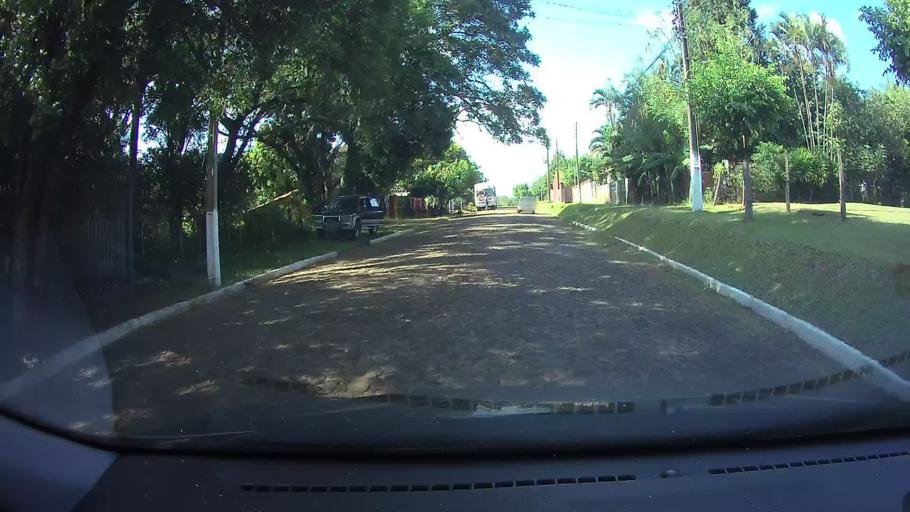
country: PY
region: Central
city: Limpio
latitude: -25.2518
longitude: -57.4707
